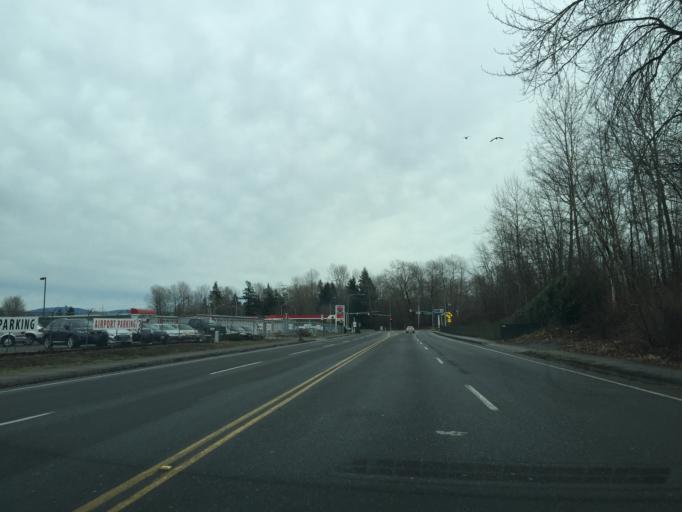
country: US
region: Washington
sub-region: Whatcom County
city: Marietta-Alderwood
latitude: 48.7860
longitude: -122.5223
